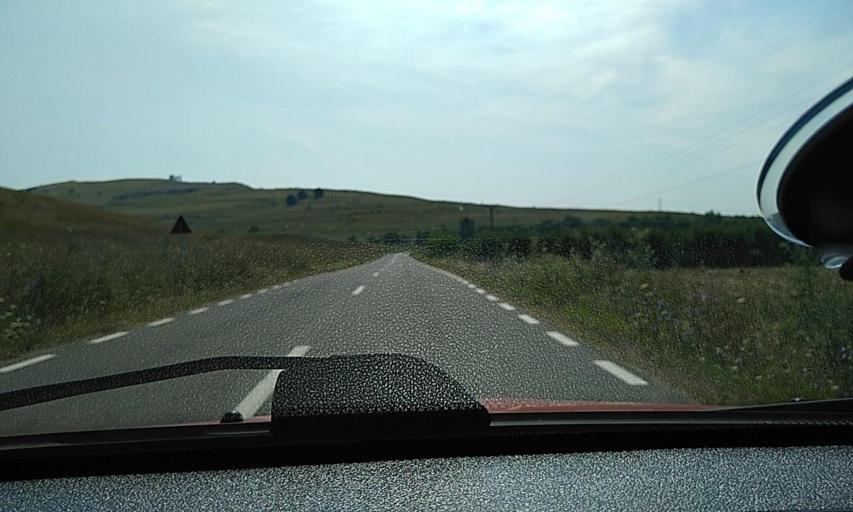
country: RO
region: Brasov
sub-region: Oras Rupea
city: Fiser
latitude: 46.0386
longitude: 25.1314
